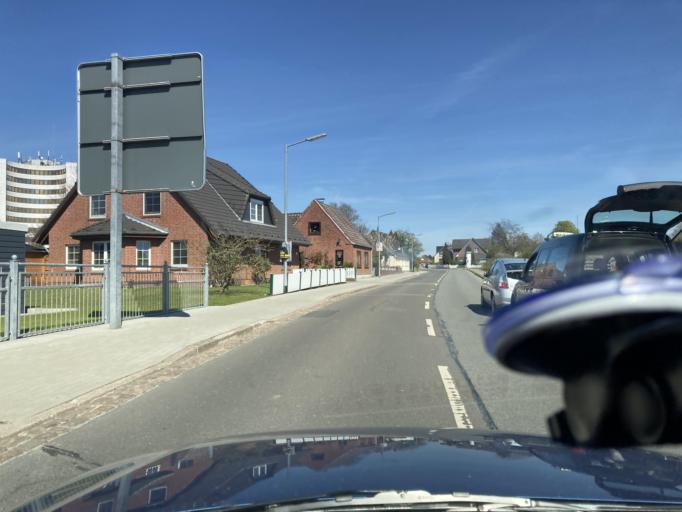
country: DE
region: Schleswig-Holstein
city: Heide
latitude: 54.1916
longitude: 9.1089
